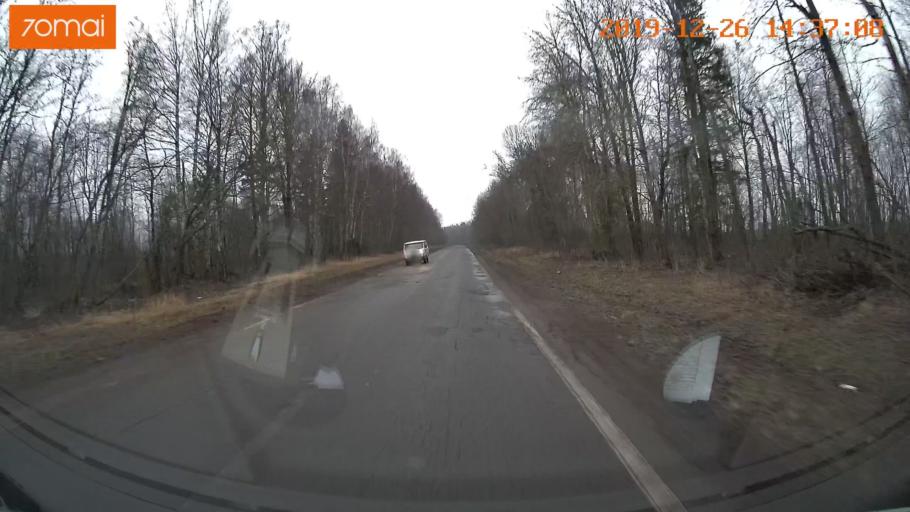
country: RU
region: Jaroslavl
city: Poshekhon'ye
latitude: 58.4049
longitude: 38.9734
